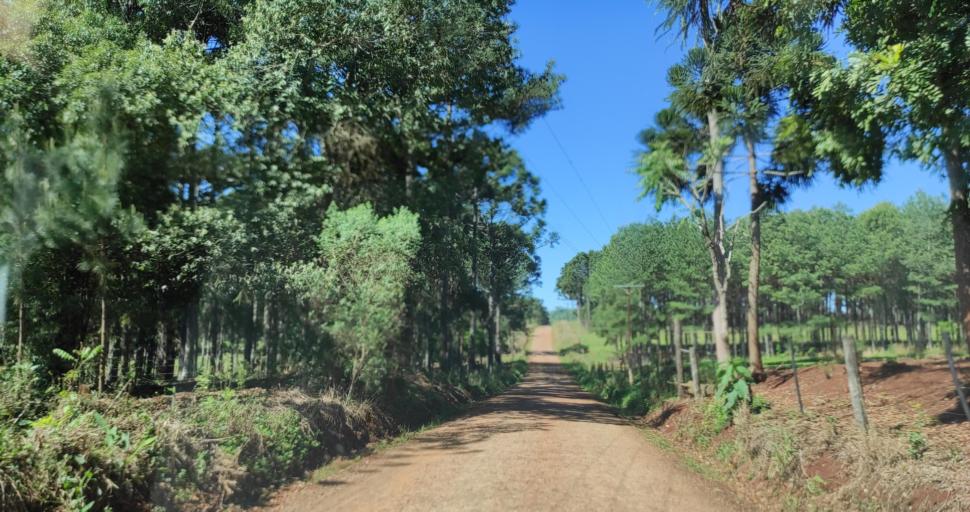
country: AR
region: Misiones
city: Capiovi
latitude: -26.9347
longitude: -55.0069
